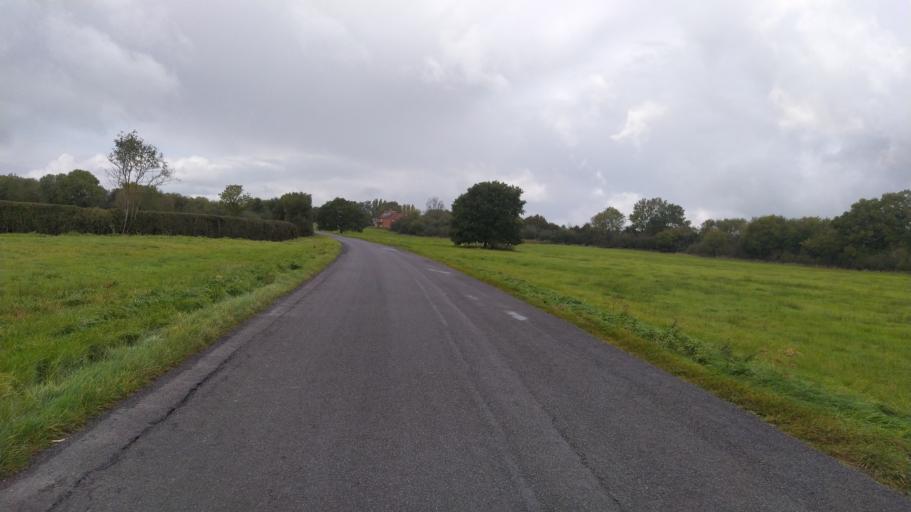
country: GB
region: England
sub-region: Dorset
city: Shaftesbury
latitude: 51.0446
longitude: -2.1756
